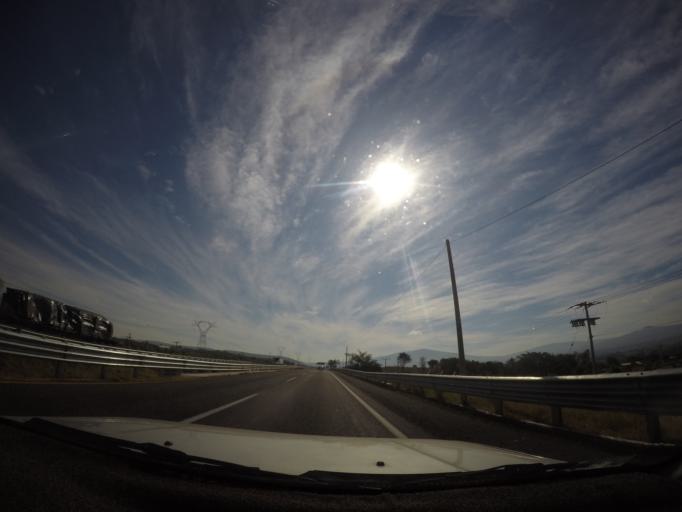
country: MX
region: Puebla
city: Necaxa
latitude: 20.2398
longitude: -98.0349
